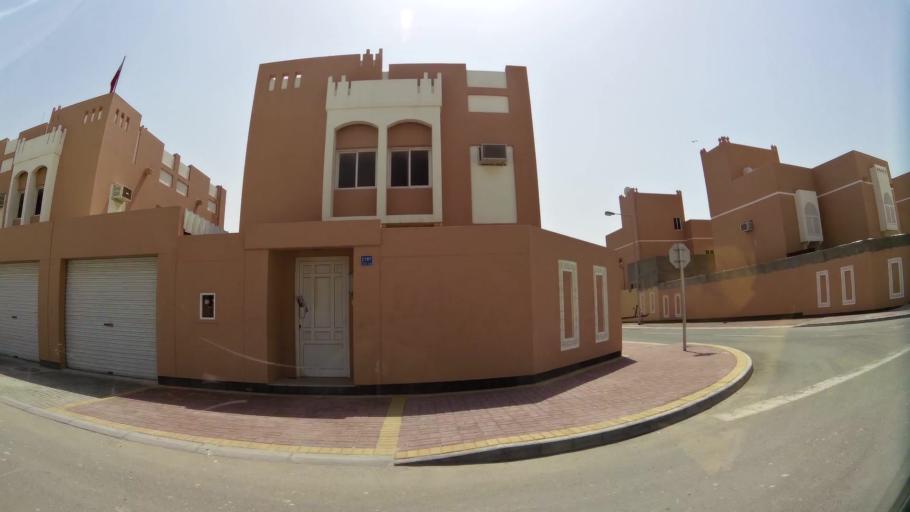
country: BH
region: Manama
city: Jidd Hafs
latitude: 26.2194
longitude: 50.4487
